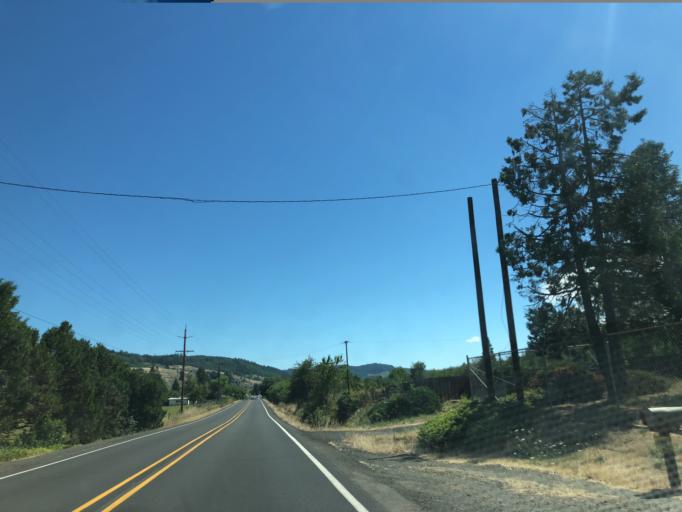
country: US
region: Oregon
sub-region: Douglas County
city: Yoncalla
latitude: 43.5716
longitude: -123.2809
